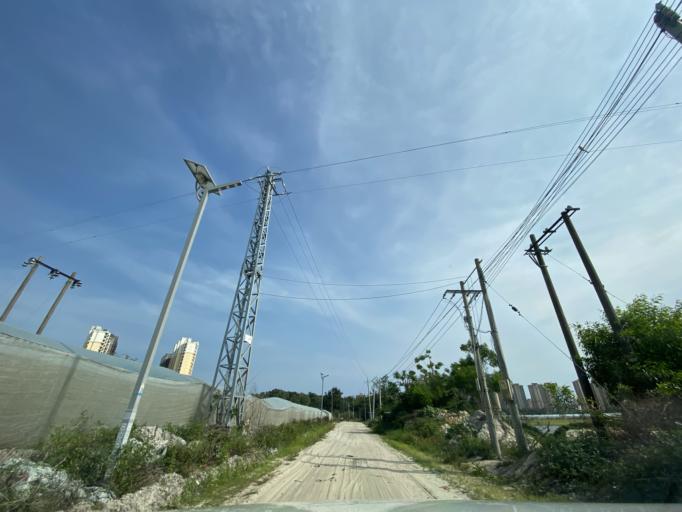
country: CN
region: Hainan
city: Yingzhou
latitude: 18.4060
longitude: 109.8369
